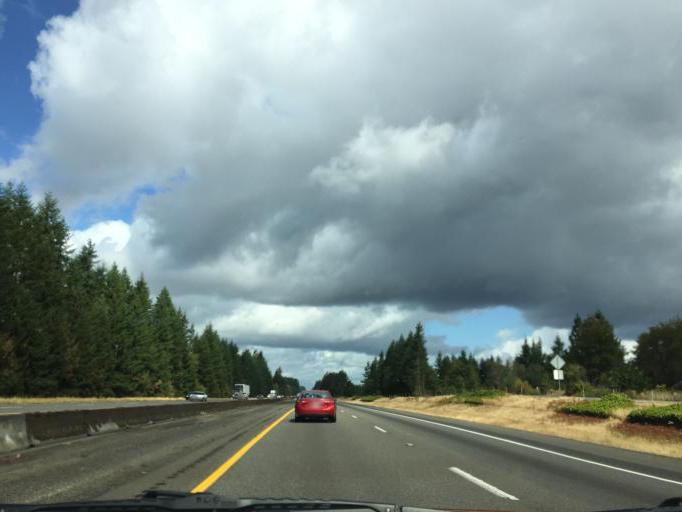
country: US
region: Washington
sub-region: Lewis County
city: Winlock
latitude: 46.4978
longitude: -122.8766
